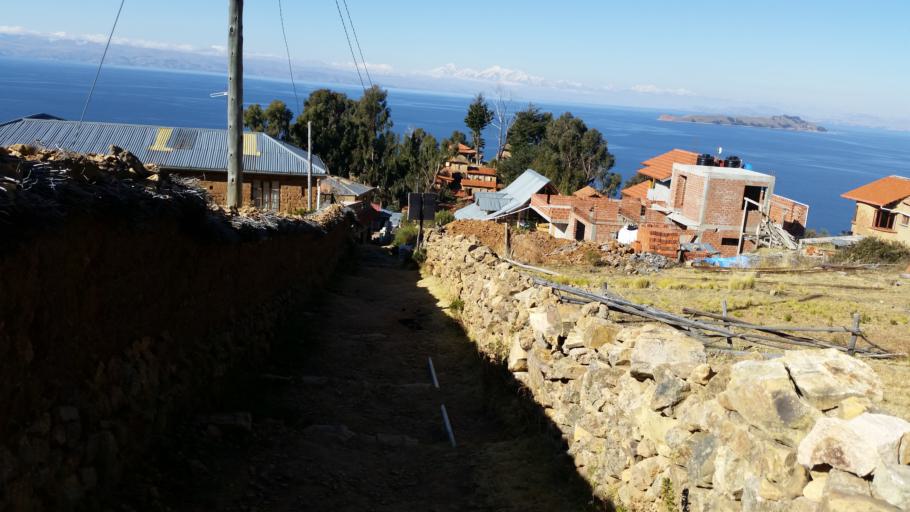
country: BO
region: La Paz
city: Yumani
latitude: -16.0372
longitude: -69.1476
